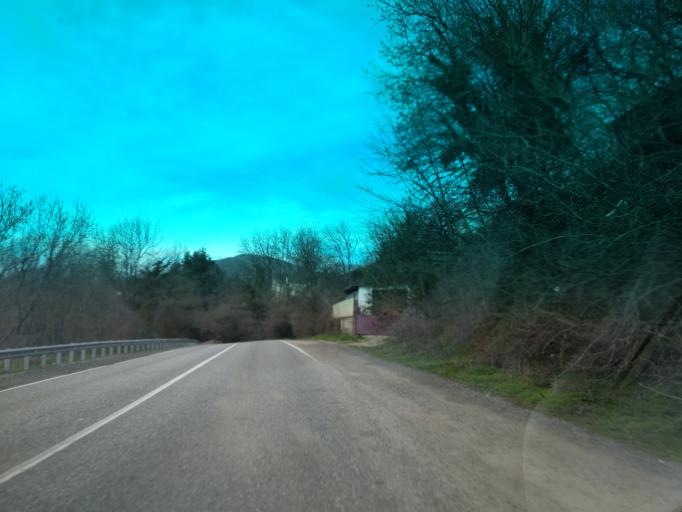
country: RU
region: Krasnodarskiy
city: Shepsi
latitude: 44.0738
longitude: 39.1359
